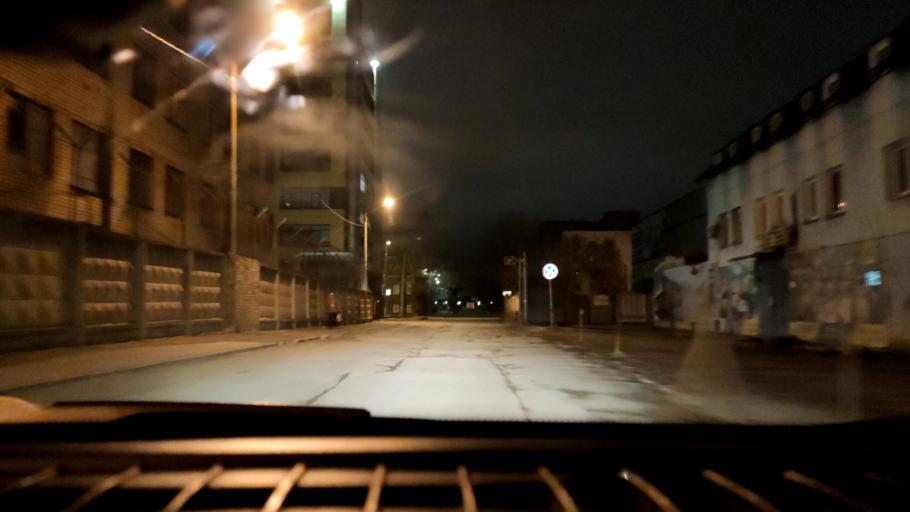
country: RU
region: Perm
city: Perm
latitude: 58.0102
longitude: 56.1865
